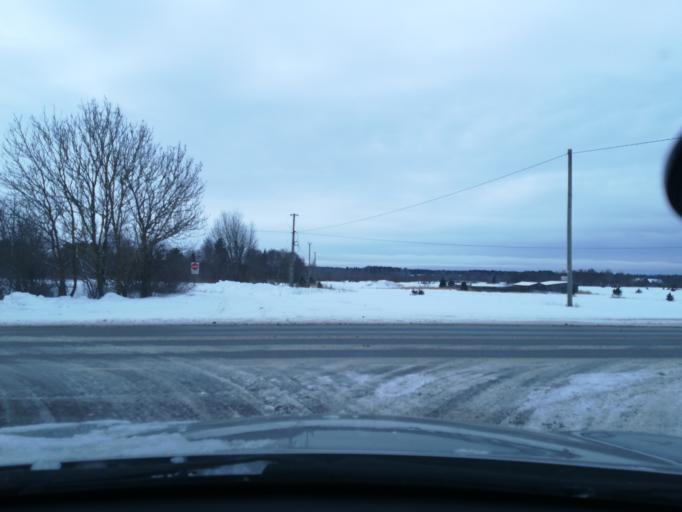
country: EE
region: Harju
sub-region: Harku vald
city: Tabasalu
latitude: 59.4423
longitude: 24.4908
